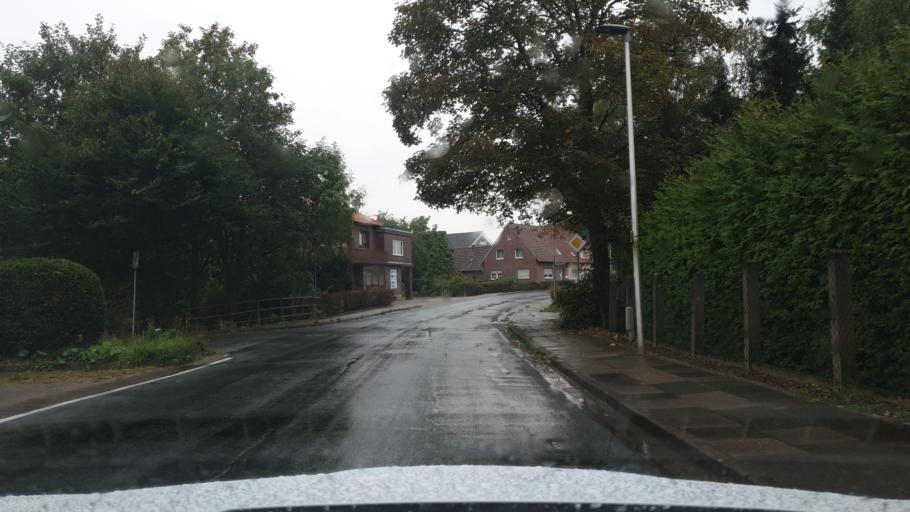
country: DE
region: North Rhine-Westphalia
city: Porta Westfalica
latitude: 52.2172
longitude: 8.8721
